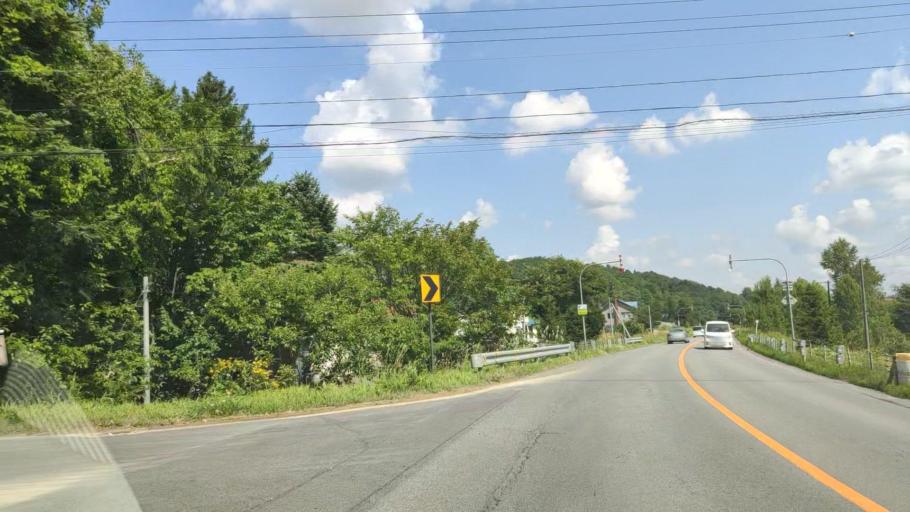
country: JP
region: Hokkaido
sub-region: Asahikawa-shi
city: Asahikawa
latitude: 43.5648
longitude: 142.4345
